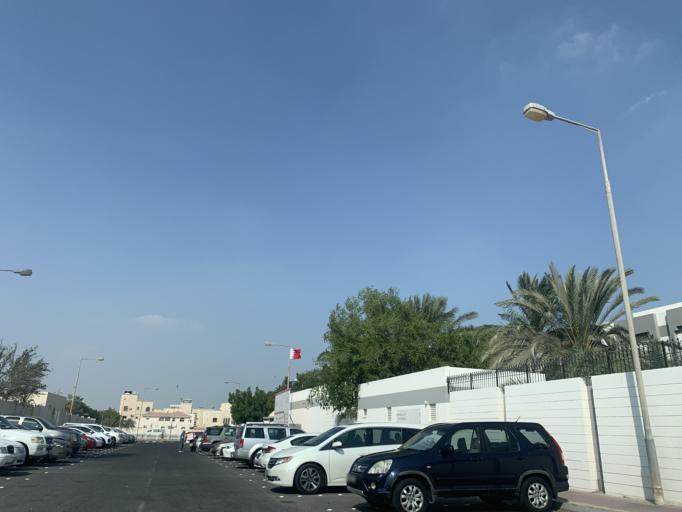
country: BH
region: Central Governorate
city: Madinat Hamad
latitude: 26.1327
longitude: 50.4957
